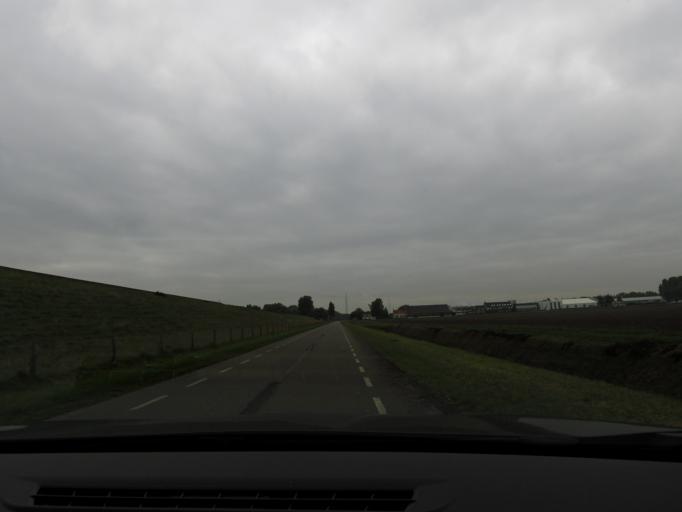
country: NL
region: South Holland
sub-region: Gemeente Hellevoetsluis
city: Hellevoetsluis
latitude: 51.8191
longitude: 4.1655
